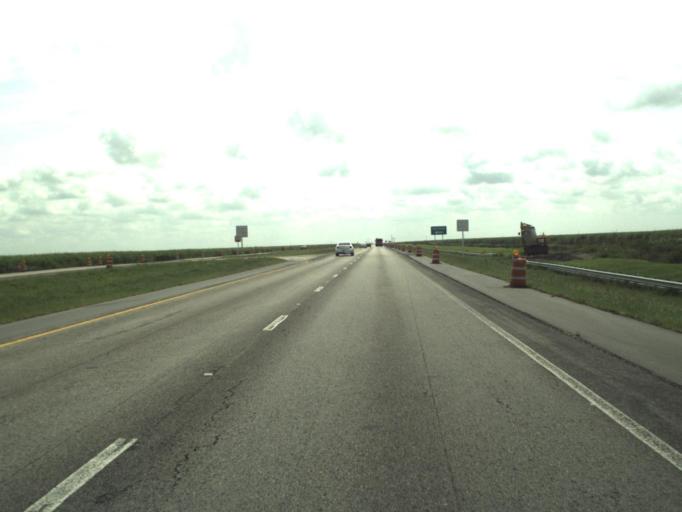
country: US
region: Florida
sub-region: Palm Beach County
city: Belle Glade
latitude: 26.7260
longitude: -80.5960
